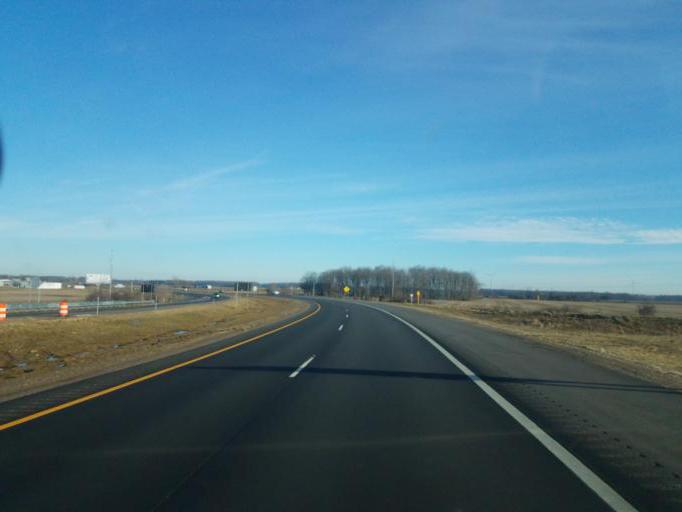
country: US
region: Michigan
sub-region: Gratiot County
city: Ithaca
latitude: 43.2936
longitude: -84.5831
